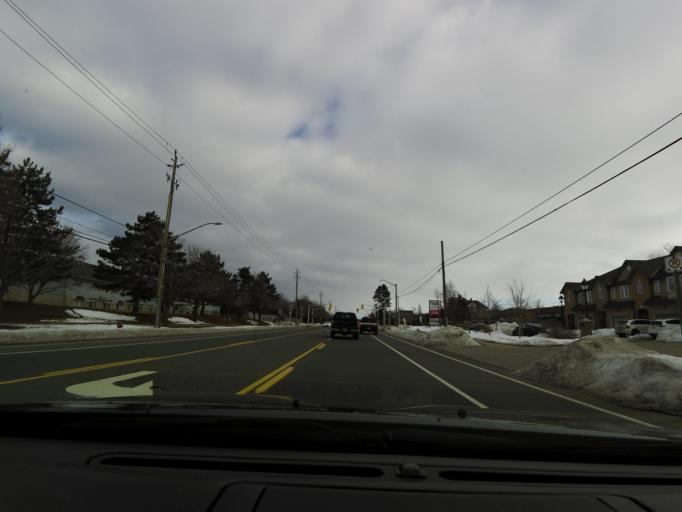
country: CA
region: Ontario
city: Hamilton
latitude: 43.2150
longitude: -79.7106
